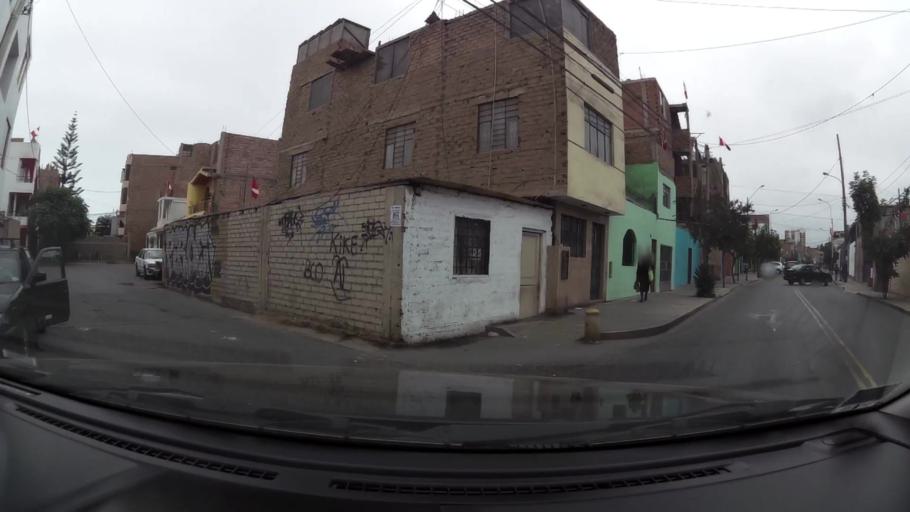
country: PE
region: Lima
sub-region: Lima
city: Surco
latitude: -12.1498
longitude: -77.0123
